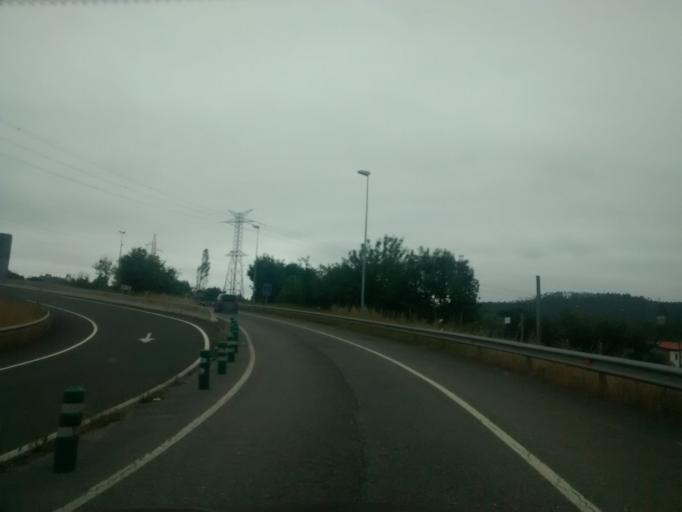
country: ES
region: Cantabria
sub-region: Provincia de Cantabria
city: Luzmela
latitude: 43.3253
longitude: -4.1925
